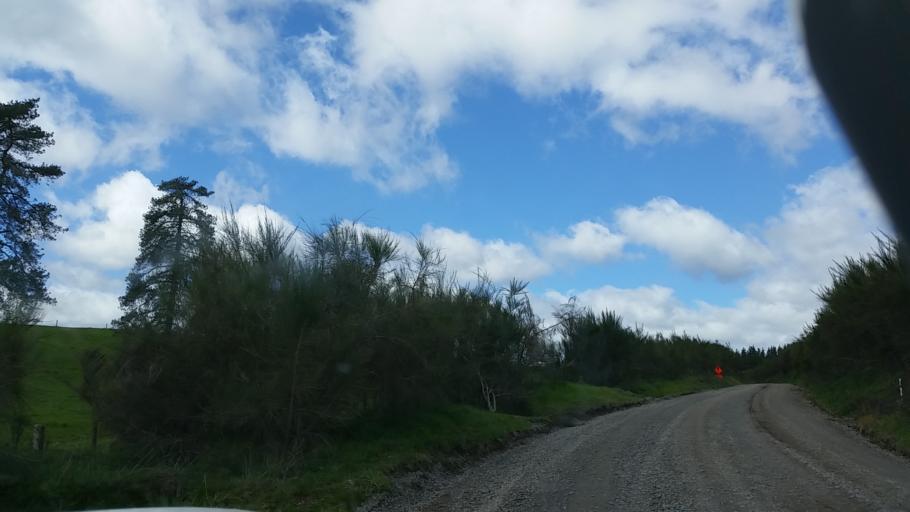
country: NZ
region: Bay of Plenty
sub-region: Whakatane District
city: Murupara
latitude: -38.3408
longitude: 176.5405
